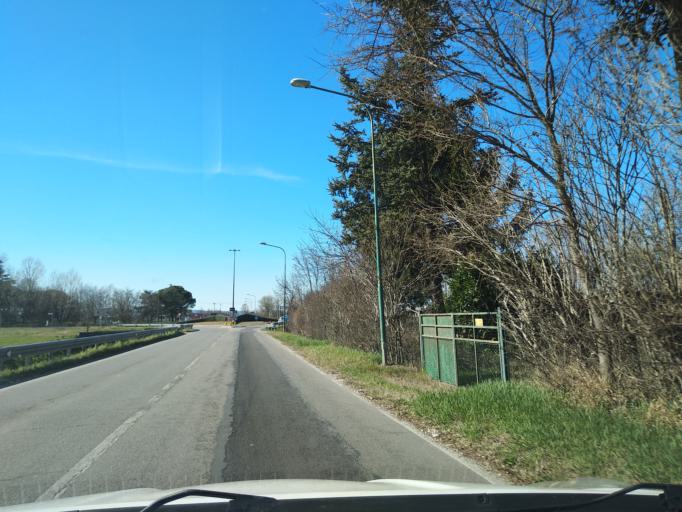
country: IT
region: Veneto
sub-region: Provincia di Padova
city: Caselle
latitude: 45.4134
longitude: 11.8053
